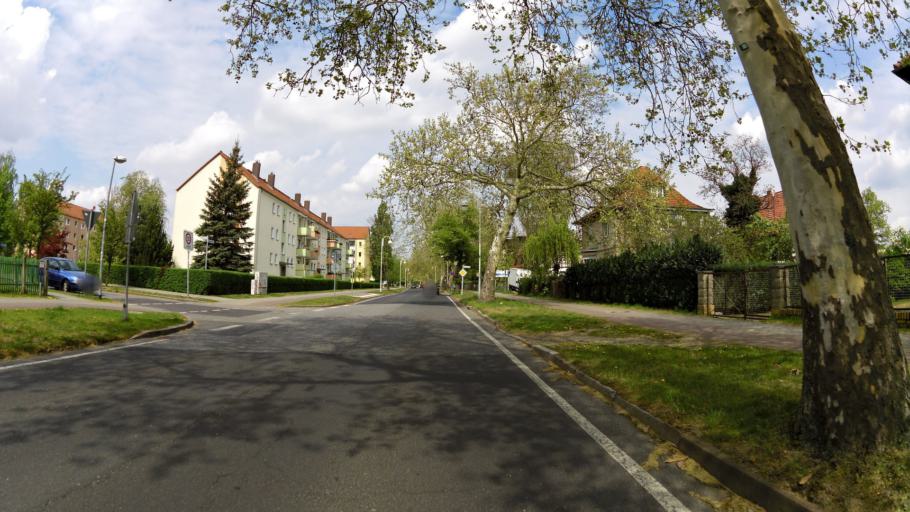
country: DE
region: Berlin
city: Lichtenrade
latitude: 52.3634
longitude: 13.4119
